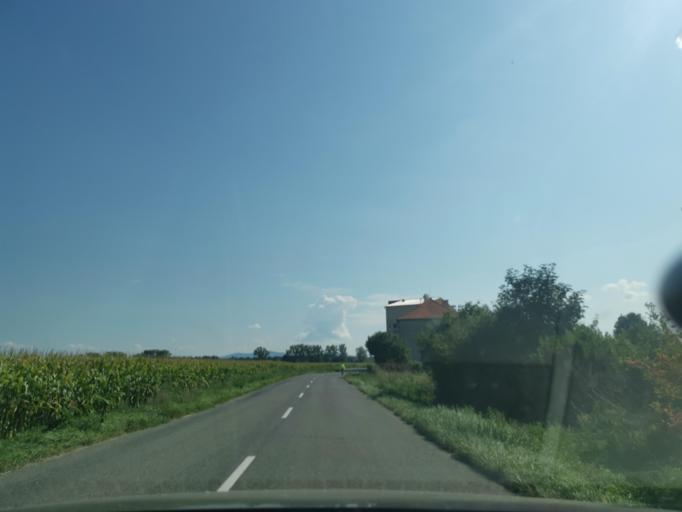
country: SK
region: Trnavsky
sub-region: Okres Senica
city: Senica
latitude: 48.6685
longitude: 17.2597
